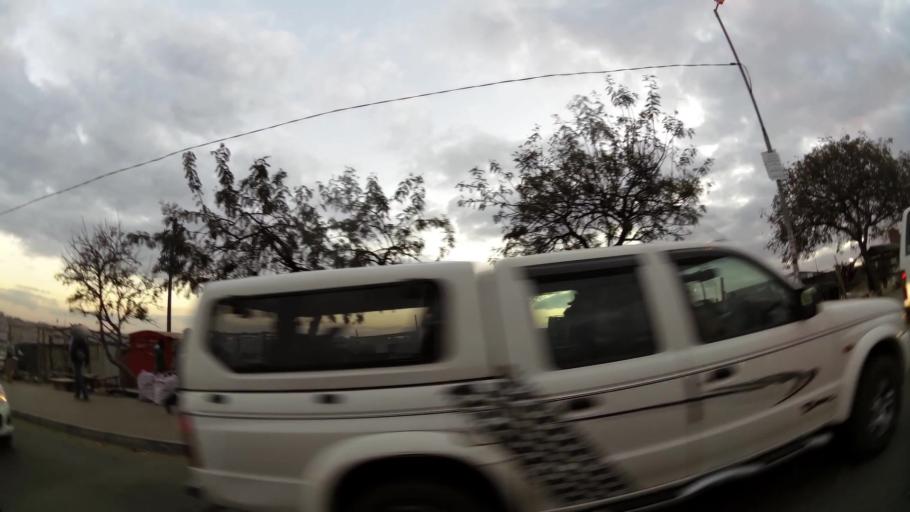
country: ZA
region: Gauteng
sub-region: City of Johannesburg Metropolitan Municipality
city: Midrand
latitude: -25.9894
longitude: 28.1749
